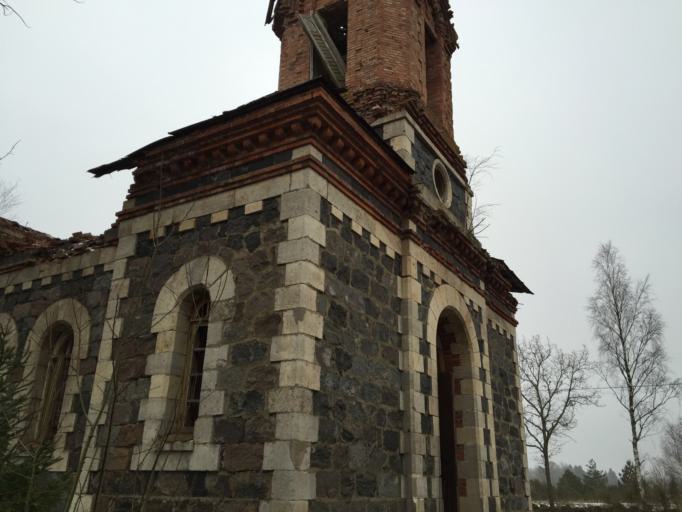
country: EE
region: Laeaene
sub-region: Lihula vald
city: Lihula
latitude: 58.6219
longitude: 23.6306
